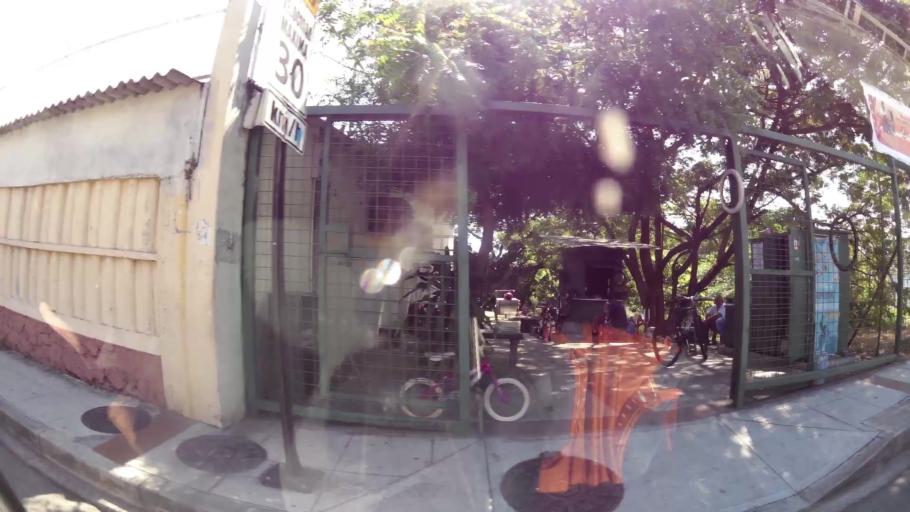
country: EC
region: Guayas
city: Guayaquil
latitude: -2.1627
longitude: -79.9192
